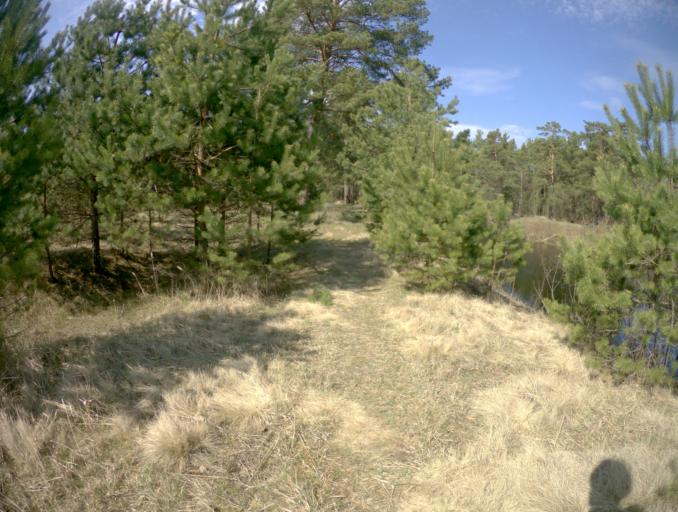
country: RU
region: Vladimir
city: Mezinovskiy
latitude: 55.5433
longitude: 40.2641
